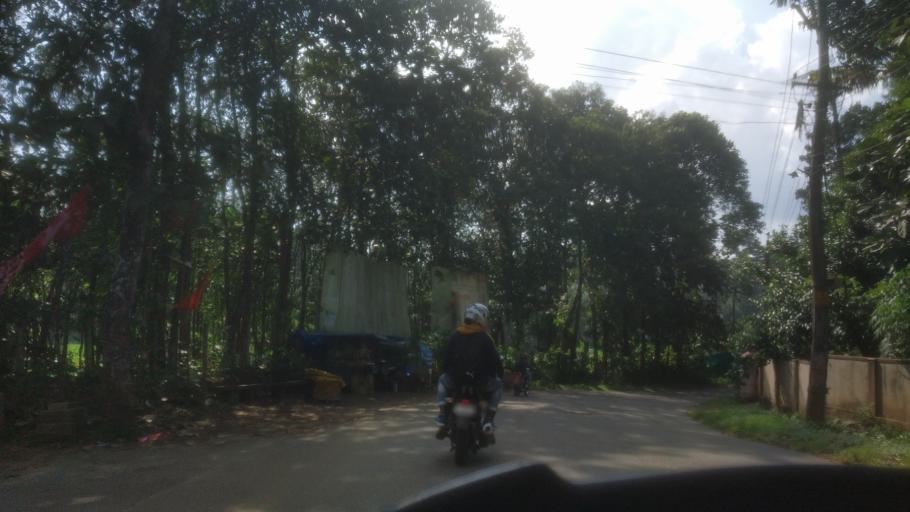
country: IN
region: Kerala
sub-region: Ernakulam
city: Muvattupula
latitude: 9.9994
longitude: 76.6315
